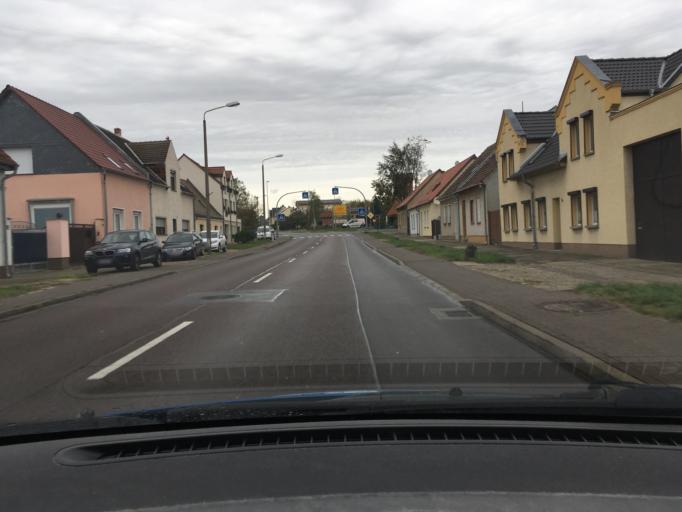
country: DE
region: Saxony-Anhalt
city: Zerbst
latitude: 51.9706
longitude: 12.0710
